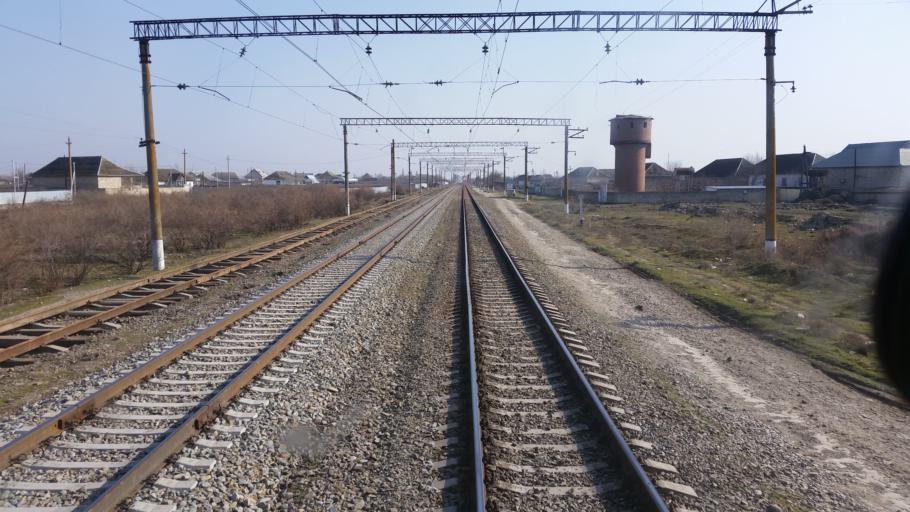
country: AZ
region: Sabirabad
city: Sabirabad
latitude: 40.2607
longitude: 48.4144
